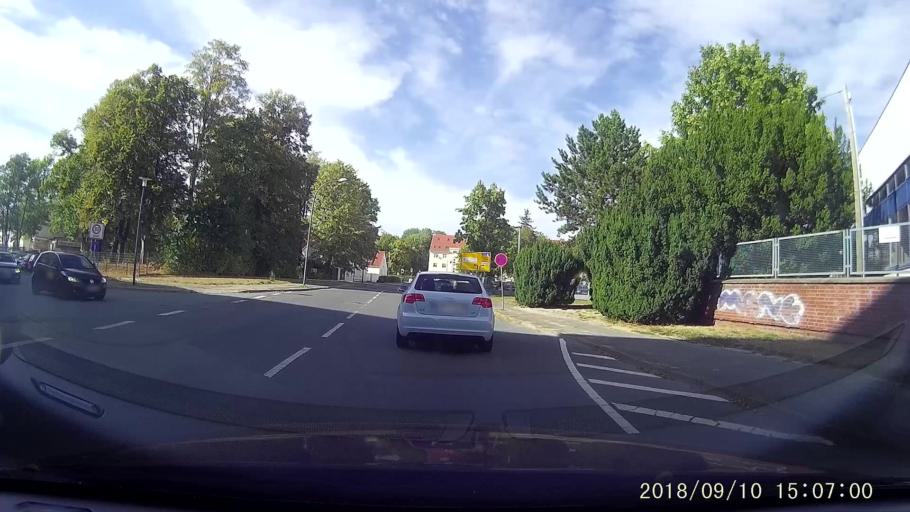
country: DE
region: Saxony
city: Goerlitz
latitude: 51.1469
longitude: 14.9484
